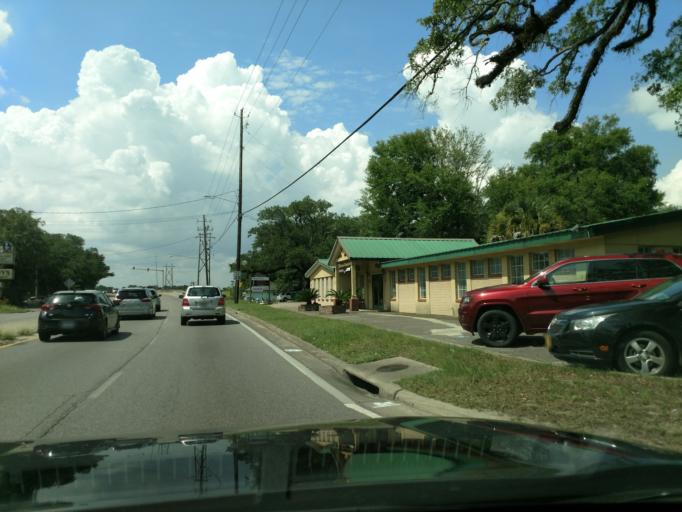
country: US
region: Mississippi
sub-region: Jackson County
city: Ocean Springs
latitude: 30.4175
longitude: -88.8275
